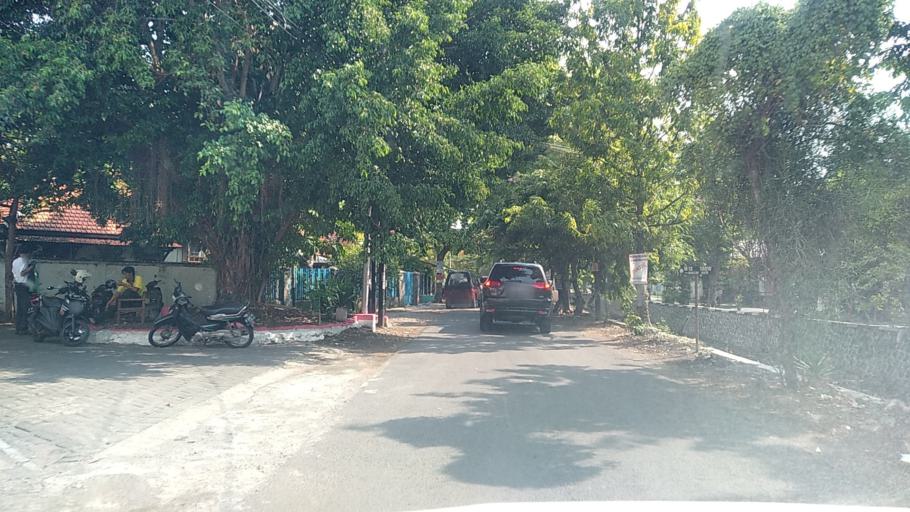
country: ID
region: Central Java
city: Semarang
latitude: -6.9932
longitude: 110.4362
